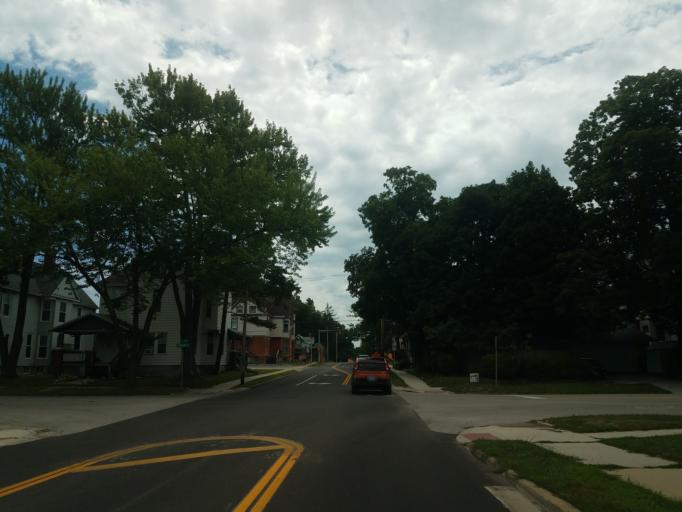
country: US
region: Illinois
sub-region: McLean County
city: Bloomington
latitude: 40.4790
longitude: -88.9846
